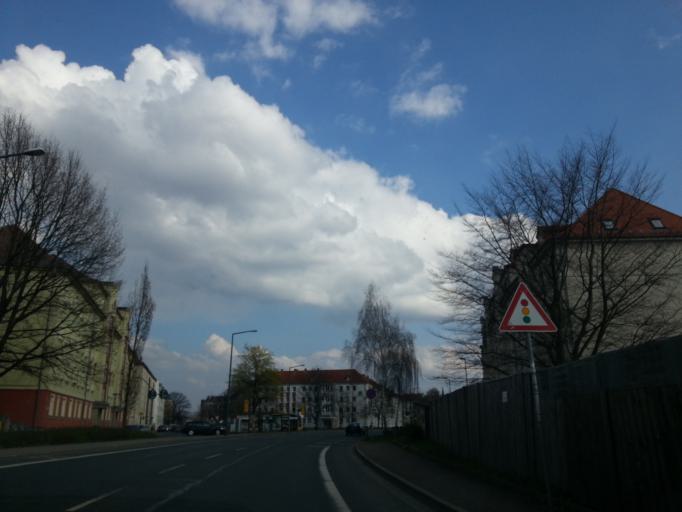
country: DE
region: Saxony
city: Dresden
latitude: 51.0826
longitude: 13.7054
